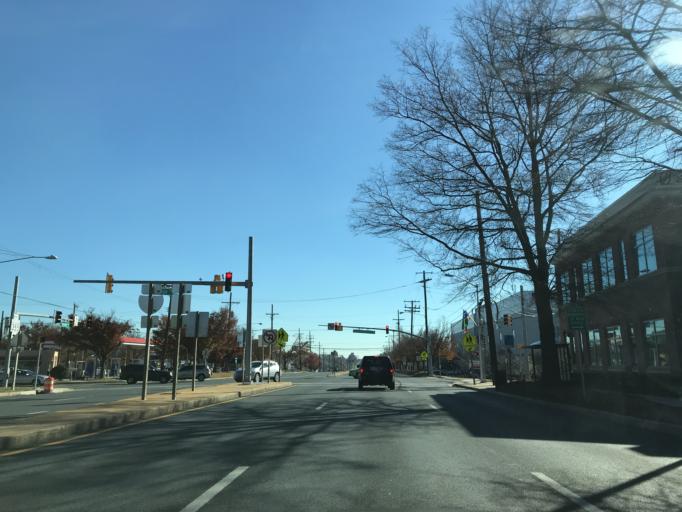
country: US
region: Maryland
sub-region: Montgomery County
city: Rockville
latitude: 39.0808
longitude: -77.1448
